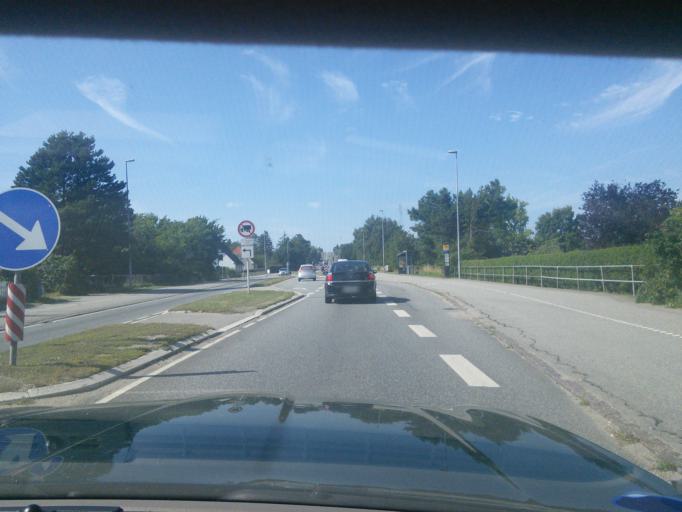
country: DK
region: Capital Region
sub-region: Halsnaes Kommune
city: Frederiksvaerk
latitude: 55.9480
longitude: 12.0463
